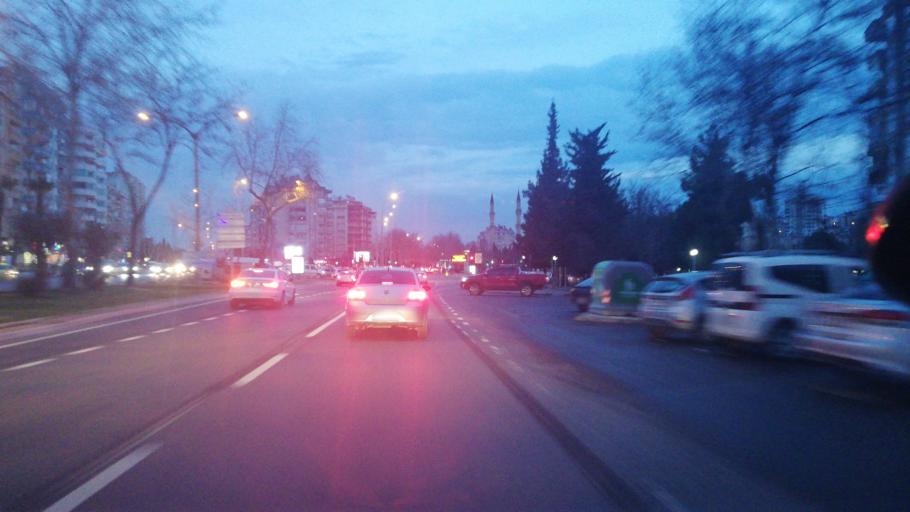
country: TR
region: Kahramanmaras
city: Kahramanmaras
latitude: 37.5867
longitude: 36.8965
